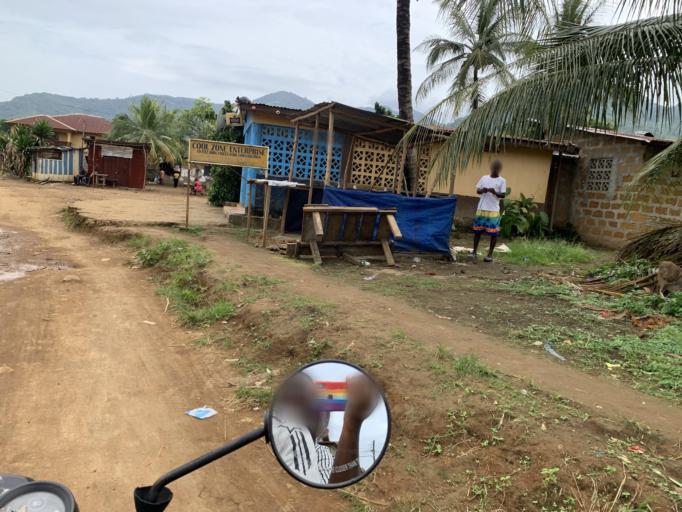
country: SL
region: Western Area
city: Hastings
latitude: 8.3772
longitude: -13.1339
